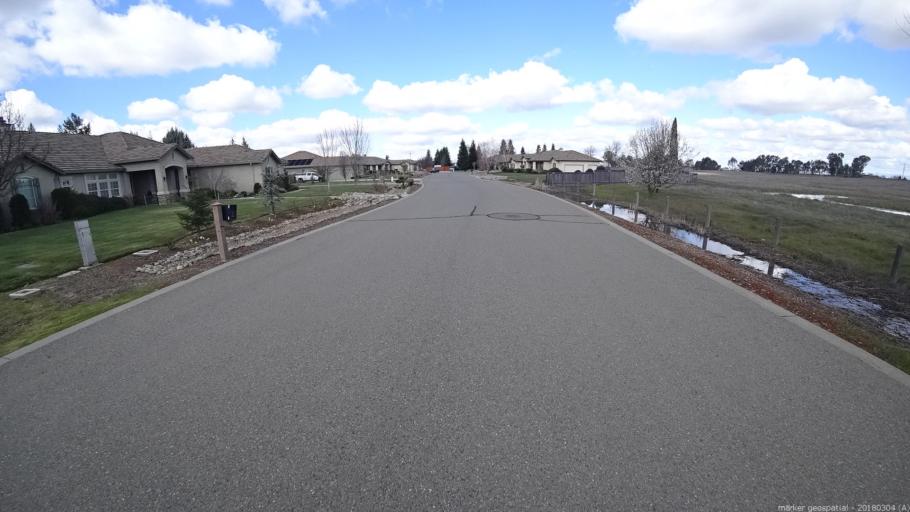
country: US
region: California
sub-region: Sacramento County
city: Vineyard
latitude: 38.4643
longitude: -121.3018
